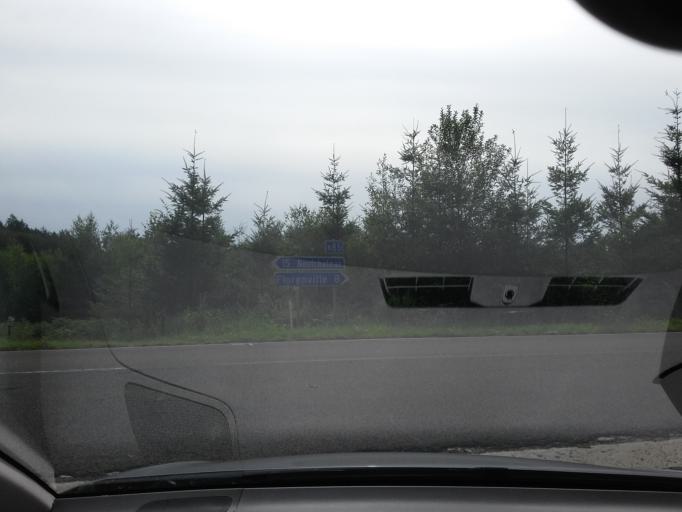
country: BE
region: Wallonia
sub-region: Province du Luxembourg
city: Chiny
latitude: 49.7515
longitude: 5.3131
